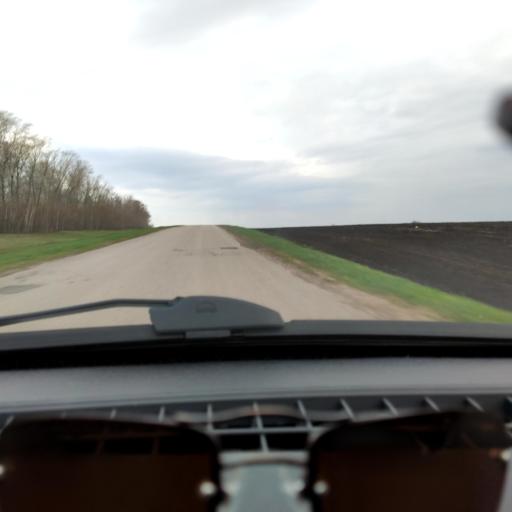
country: RU
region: Bashkortostan
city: Ulukulevo
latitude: 54.4567
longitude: 56.2462
